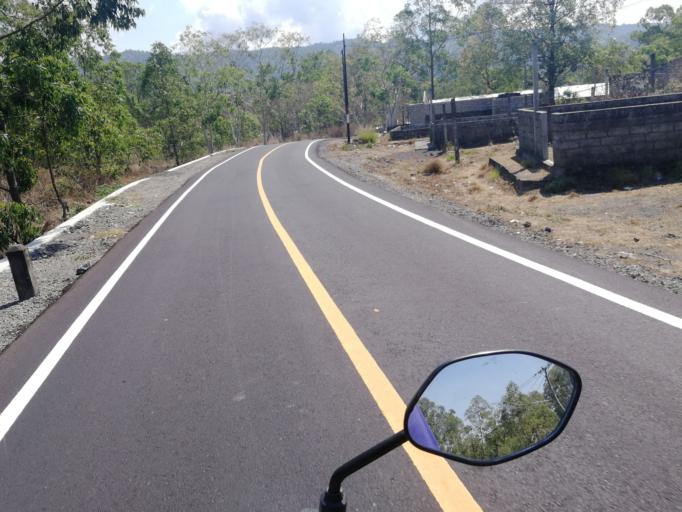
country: ID
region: Bali
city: Banjar Kedisan
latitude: -8.2650
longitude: 115.3864
